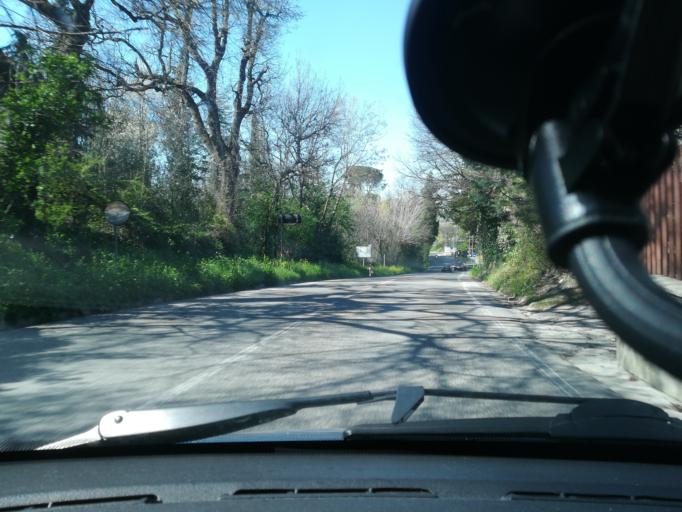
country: IT
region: The Marches
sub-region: Provincia di Macerata
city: Villa Potenza
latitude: 43.3149
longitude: 13.4331
